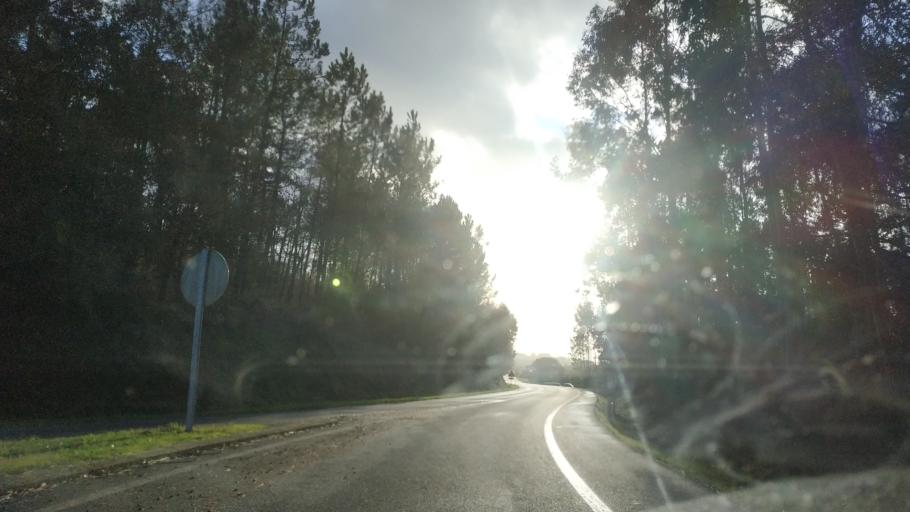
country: ES
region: Galicia
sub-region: Provincia de Pontevedra
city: Silleda
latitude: 42.7884
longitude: -8.1656
